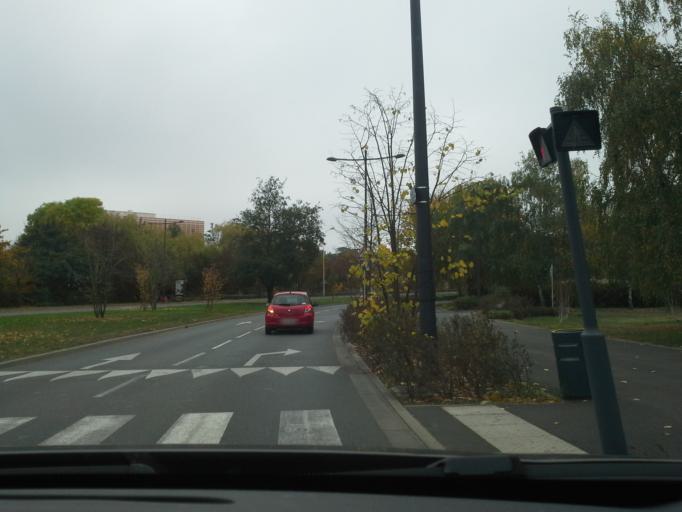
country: FR
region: Centre
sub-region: Departement d'Indre-et-Loire
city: Saint-Cyr-sur-Loire
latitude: 47.4208
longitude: 0.7038
